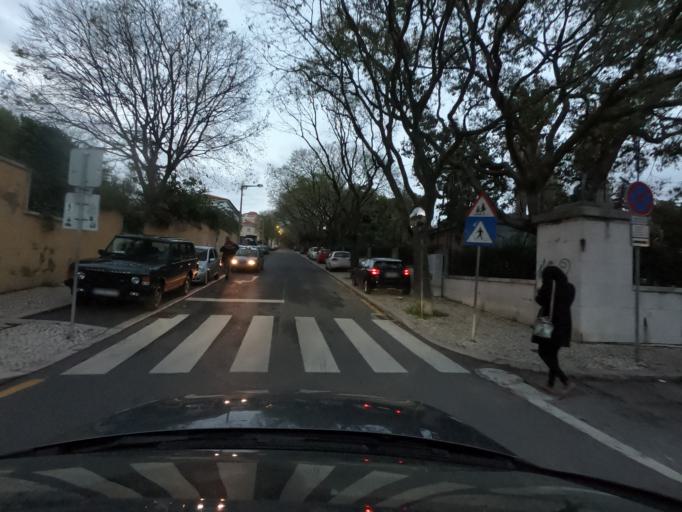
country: PT
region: Lisbon
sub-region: Oeiras
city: Alges
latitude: 38.6982
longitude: -9.2041
